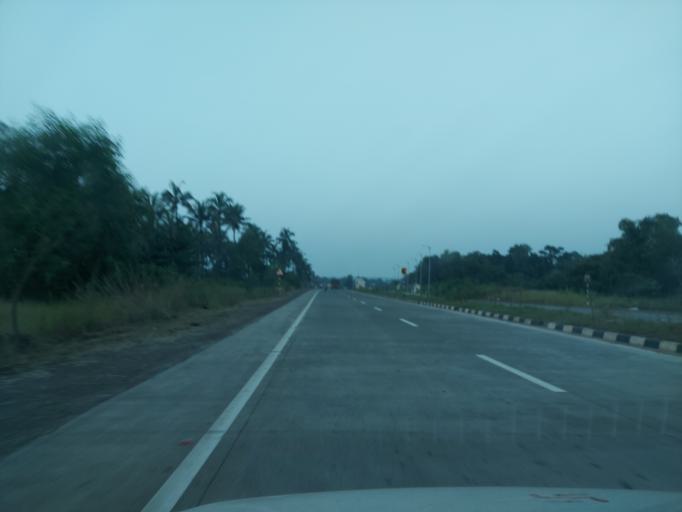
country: IN
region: Maharashtra
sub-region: Sindhudurg
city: Kudal
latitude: 16.1017
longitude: 73.7083
